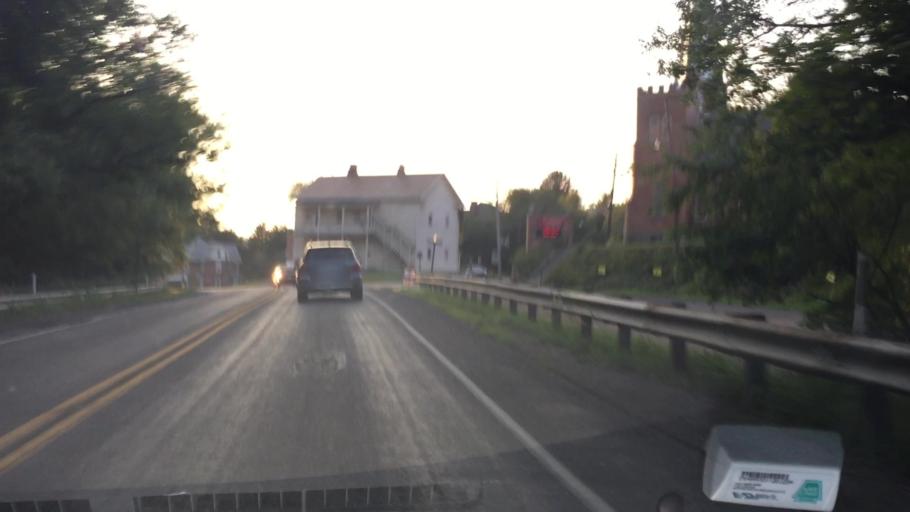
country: US
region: Pennsylvania
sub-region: Butler County
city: Evans City
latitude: 40.7666
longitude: -80.0584
